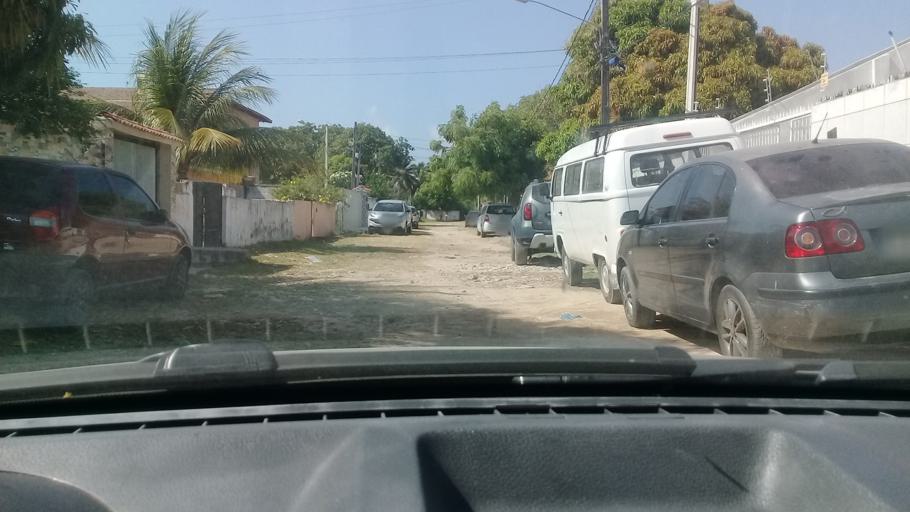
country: BR
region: Pernambuco
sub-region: Itamaraca
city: Itamaraca
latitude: -7.7562
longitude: -34.8292
